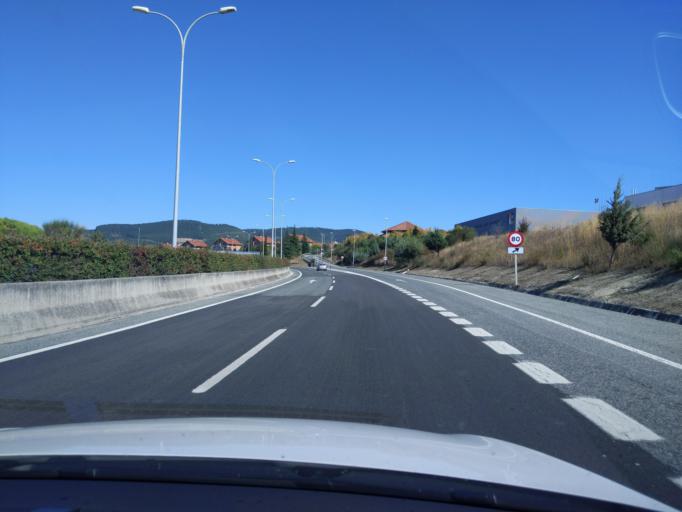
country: ES
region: Navarre
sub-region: Provincia de Navarra
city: Egues-Uharte
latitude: 42.8197
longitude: -1.5848
